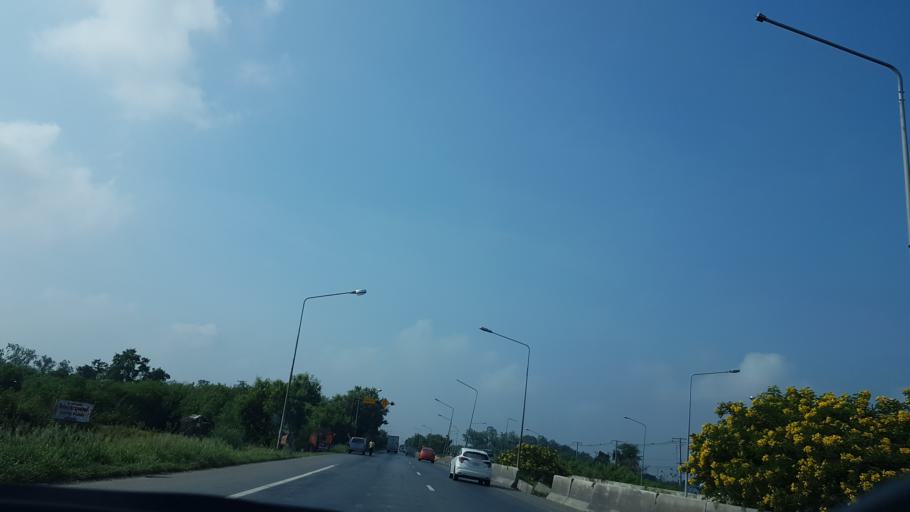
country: TH
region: Pathum Thani
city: Sam Khok
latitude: 14.1364
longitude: 100.5405
